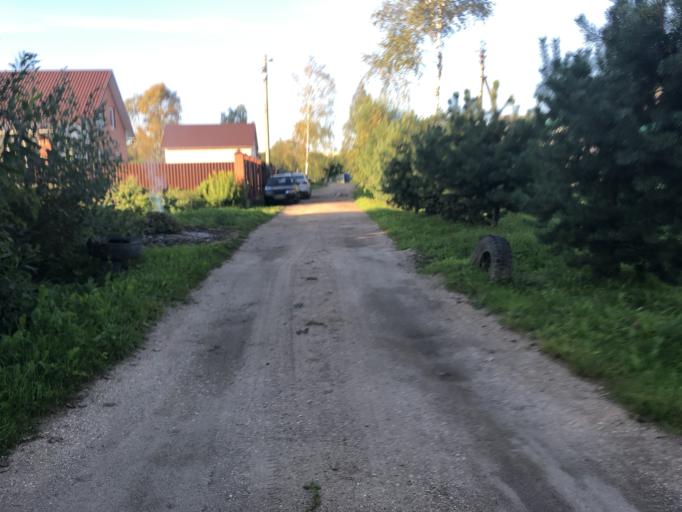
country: RU
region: Tverskaya
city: Rzhev
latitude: 56.2437
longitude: 34.3075
